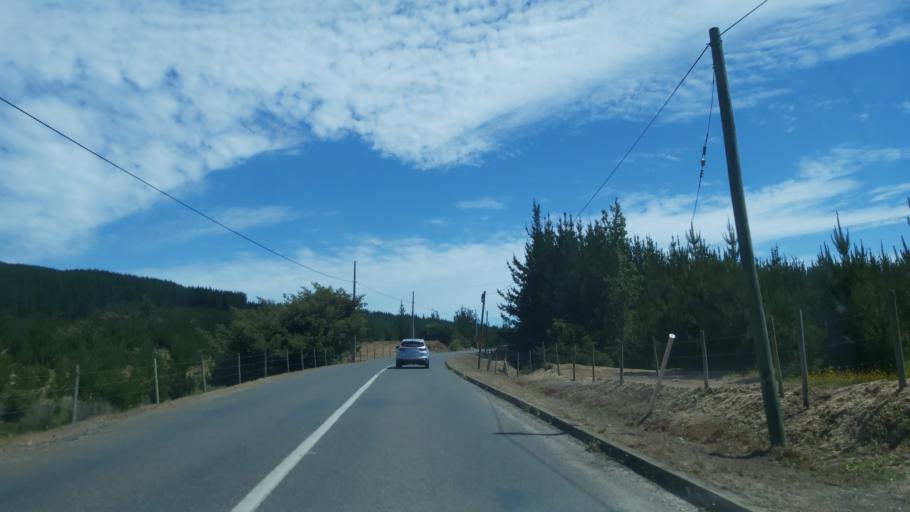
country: CL
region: Maule
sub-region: Provincia de Talca
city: Constitucion
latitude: -35.5171
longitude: -72.5304
